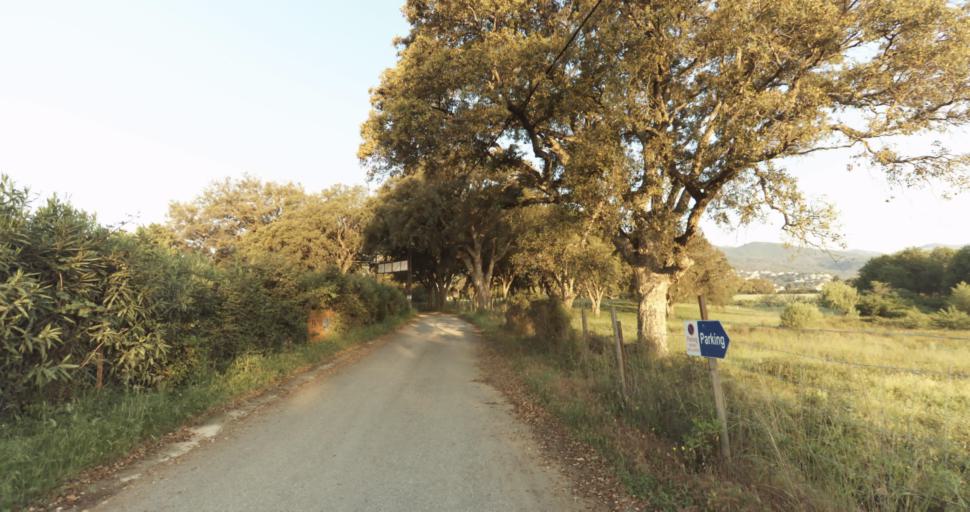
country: FR
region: Corsica
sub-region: Departement de la Haute-Corse
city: Biguglia
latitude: 42.6289
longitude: 9.4452
